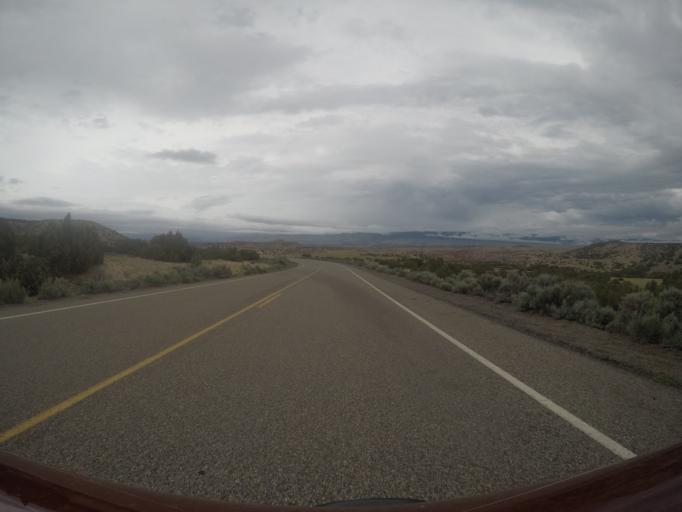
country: US
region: Wyoming
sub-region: Big Horn County
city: Lovell
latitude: 45.0617
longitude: -108.2593
